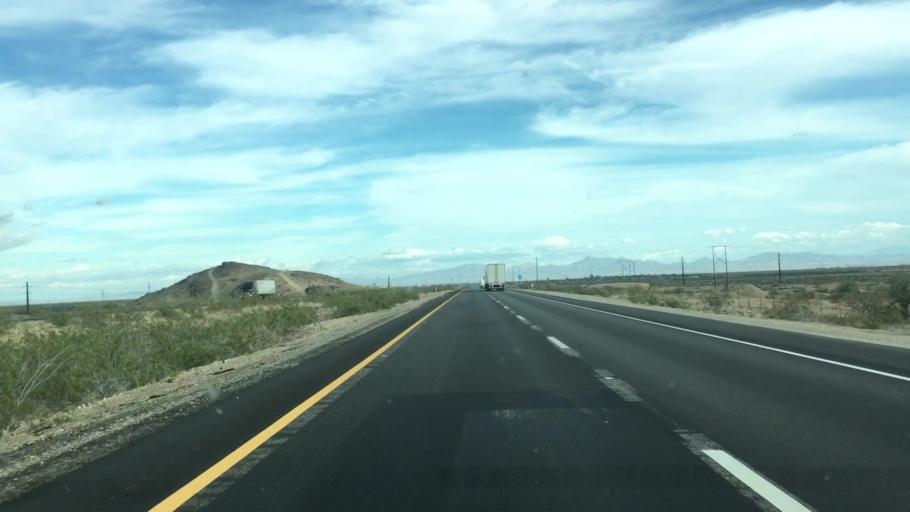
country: US
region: California
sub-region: Riverside County
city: Mesa Verde
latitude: 33.6087
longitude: -114.7660
